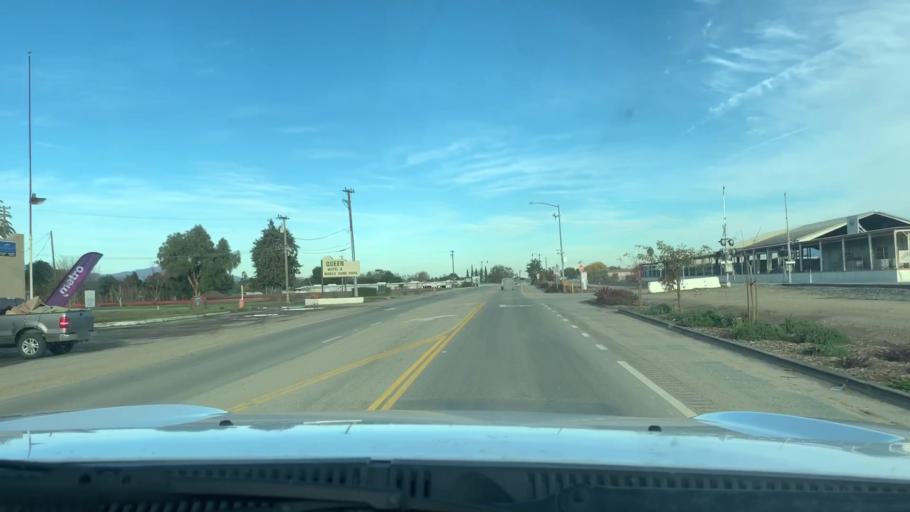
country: US
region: California
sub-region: Monterey County
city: King City
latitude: 36.2062
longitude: -121.1165
